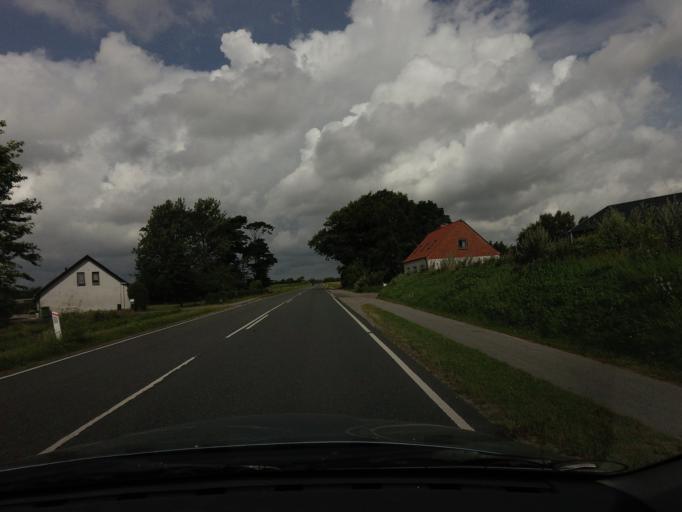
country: DK
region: North Denmark
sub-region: Hjorring Kommune
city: Tars
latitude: 57.3987
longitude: 10.0844
